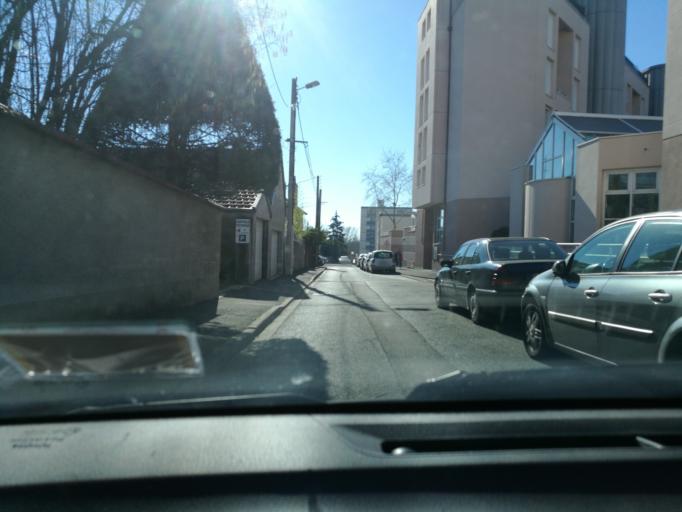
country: FR
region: Centre
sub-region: Departement du Loiret
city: Saint-Jean-de-la-Ruelle
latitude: 47.8998
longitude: 1.8825
